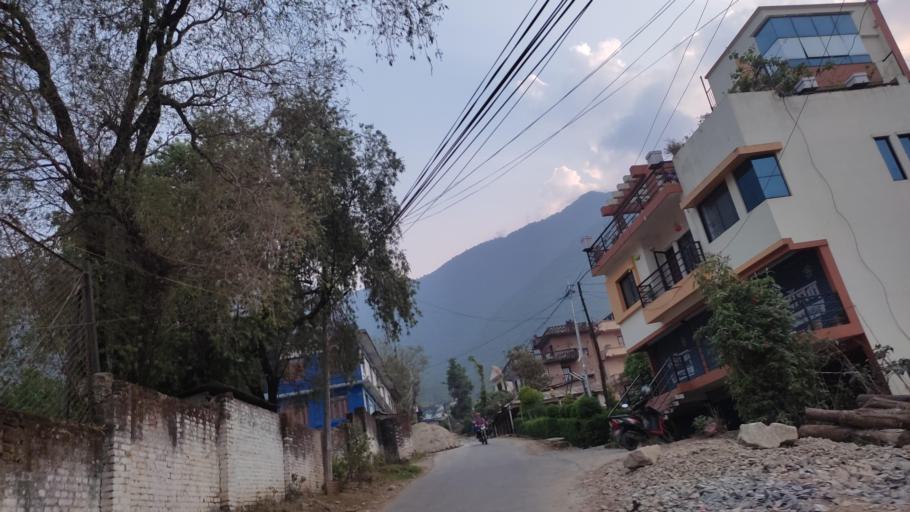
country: NP
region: Central Region
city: Kirtipur
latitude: 27.6623
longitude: 85.2540
